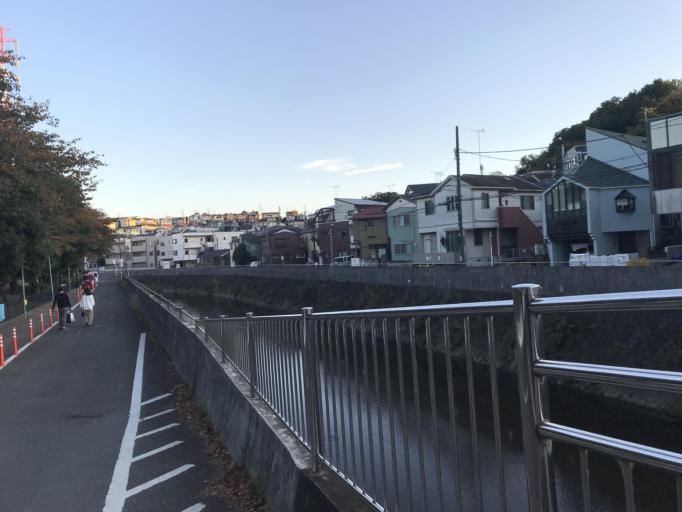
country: JP
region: Kanagawa
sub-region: Kawasaki-shi
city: Kawasaki
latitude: 35.5620
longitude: 139.6418
